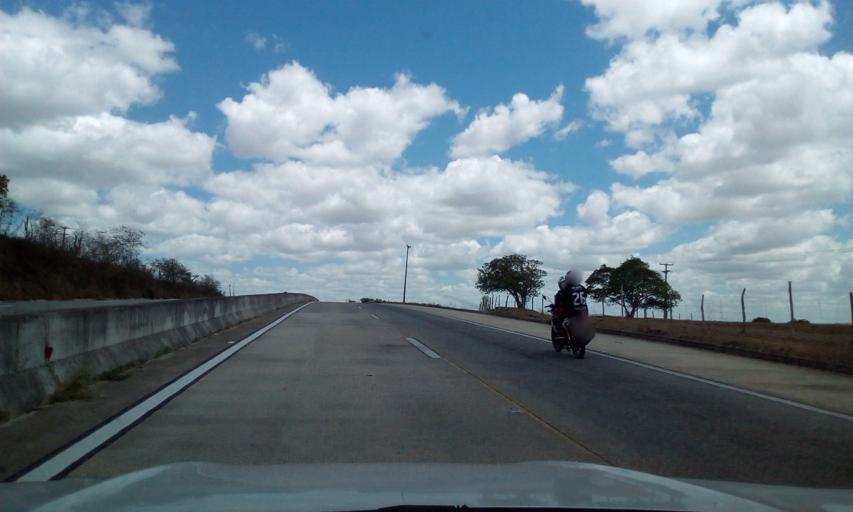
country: BR
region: Alagoas
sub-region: Porto Real Do Colegio
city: Porto Real do Colegio
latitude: -10.1372
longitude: -36.8020
